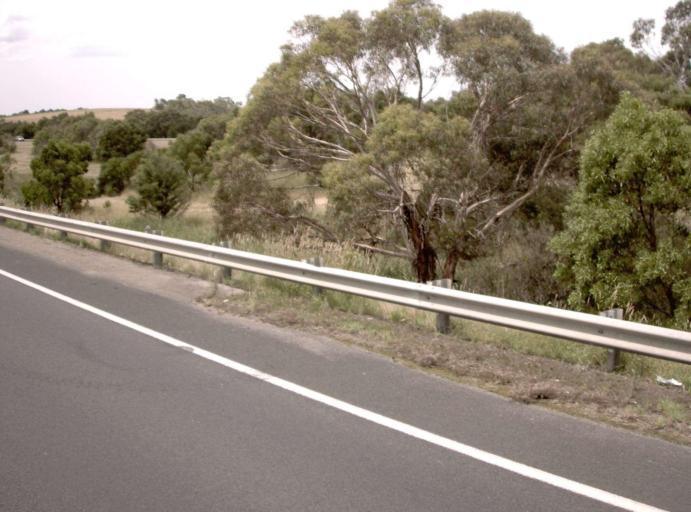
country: AU
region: Victoria
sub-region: Mornington Peninsula
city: Mount Martha
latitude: -38.2803
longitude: 145.0550
